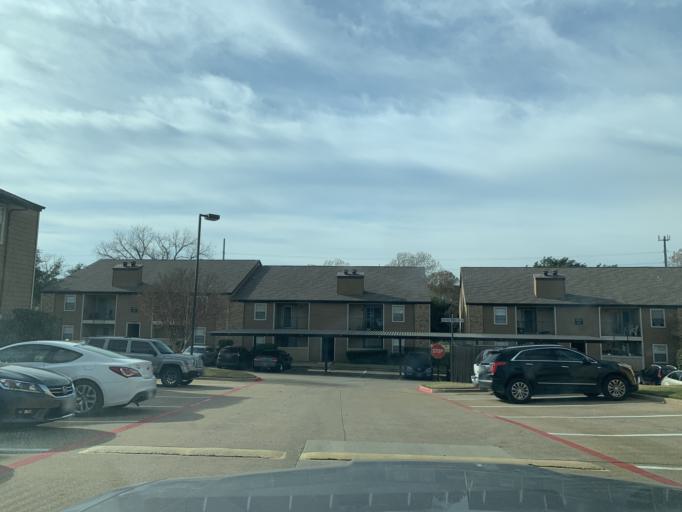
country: US
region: Texas
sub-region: Tarrant County
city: Euless
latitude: 32.7828
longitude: -97.0636
